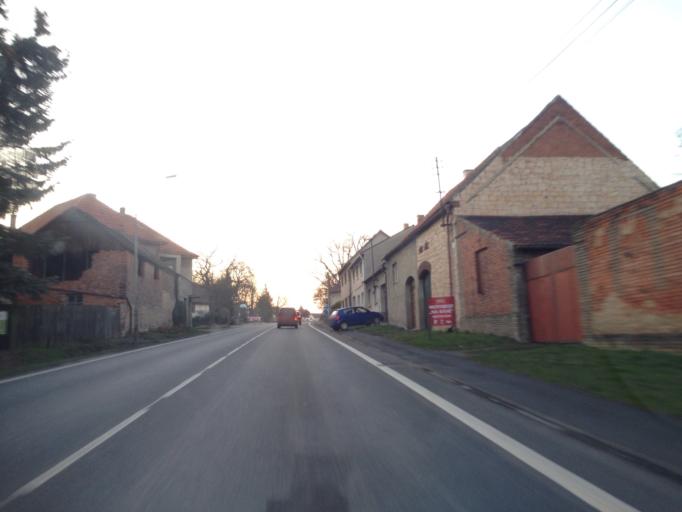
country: CZ
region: Central Bohemia
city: Revnicov
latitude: 50.1818
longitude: 13.8112
